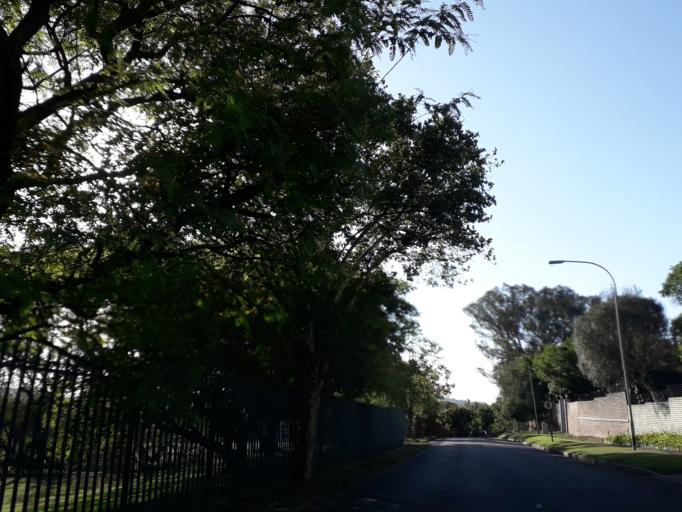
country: ZA
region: Gauteng
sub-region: City of Johannesburg Metropolitan Municipality
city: Johannesburg
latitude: -26.1550
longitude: 28.0325
